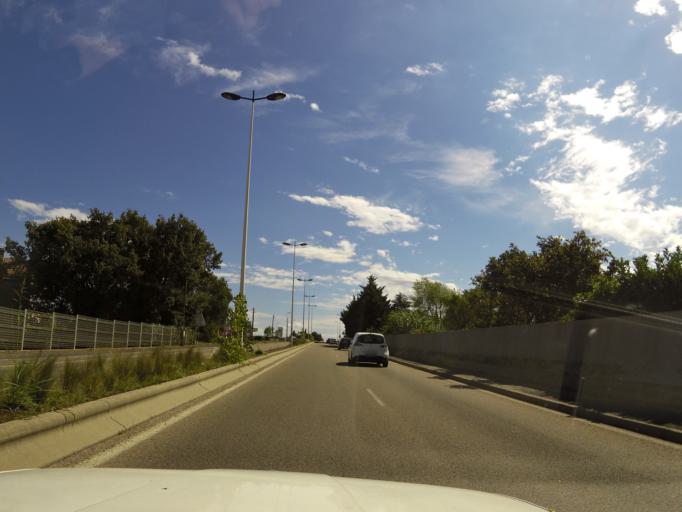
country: FR
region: Languedoc-Roussillon
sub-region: Departement du Gard
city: Ales
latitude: 44.1322
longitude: 4.1058
